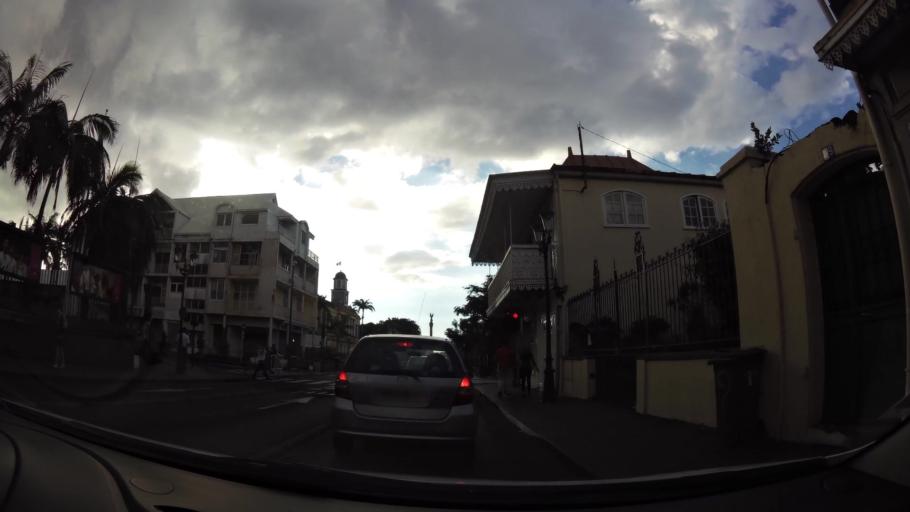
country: RE
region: Reunion
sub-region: Reunion
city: Saint-Denis
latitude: -20.8796
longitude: 55.4489
